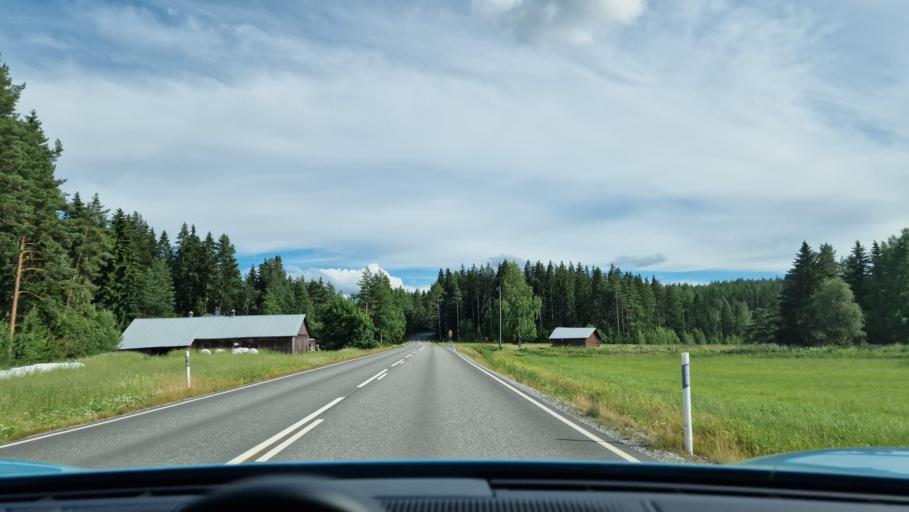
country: FI
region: Pirkanmaa
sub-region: Tampere
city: Sahalahti
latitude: 61.5677
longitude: 24.3047
